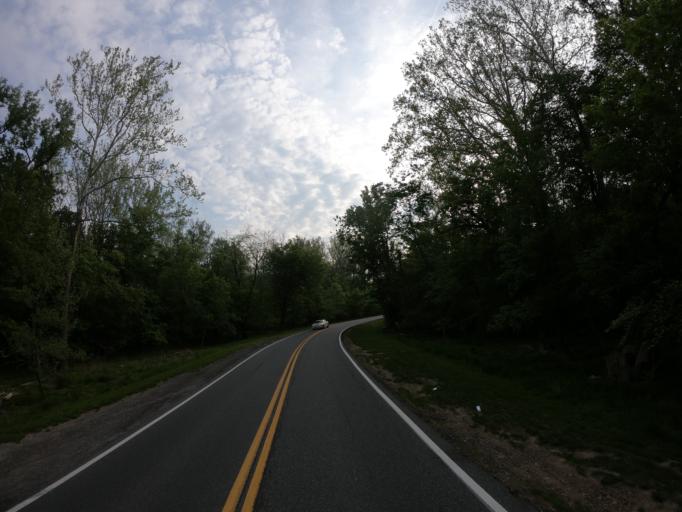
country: US
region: Maryland
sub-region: Montgomery County
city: South Kensington
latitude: 39.0262
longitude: -77.0943
